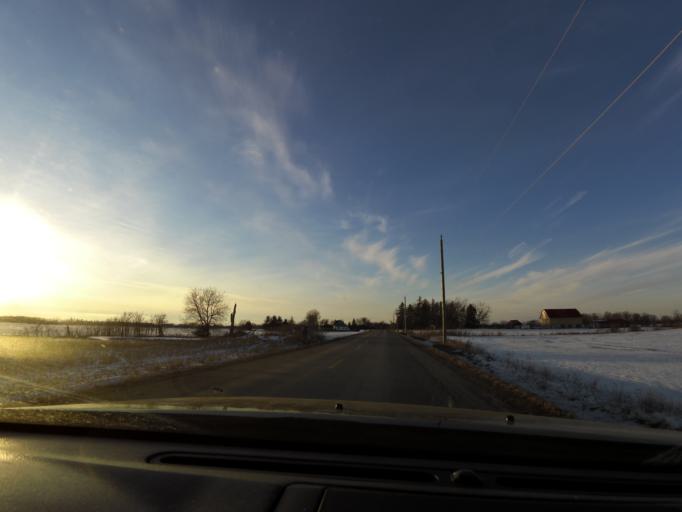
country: CA
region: Ontario
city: Hamilton
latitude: 43.1131
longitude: -79.6455
